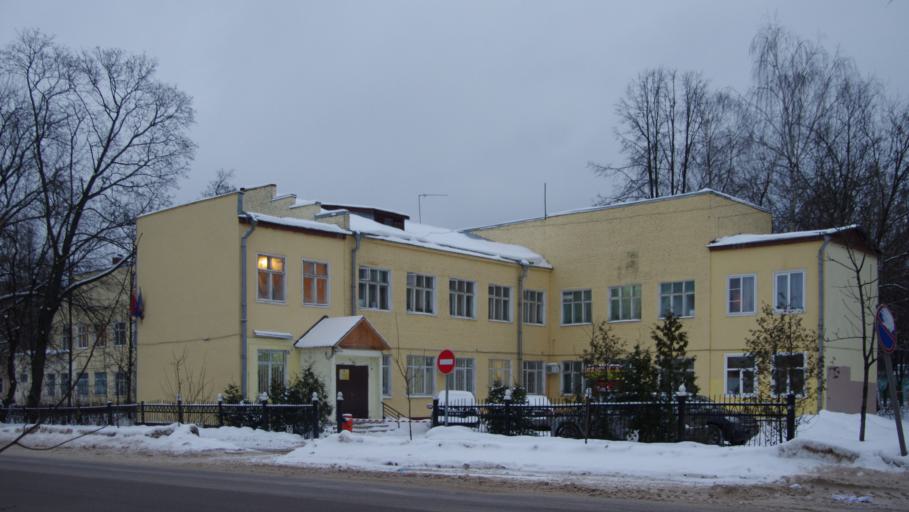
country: RU
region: Moskovskaya
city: Korolev
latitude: 55.9213
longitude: 37.8138
